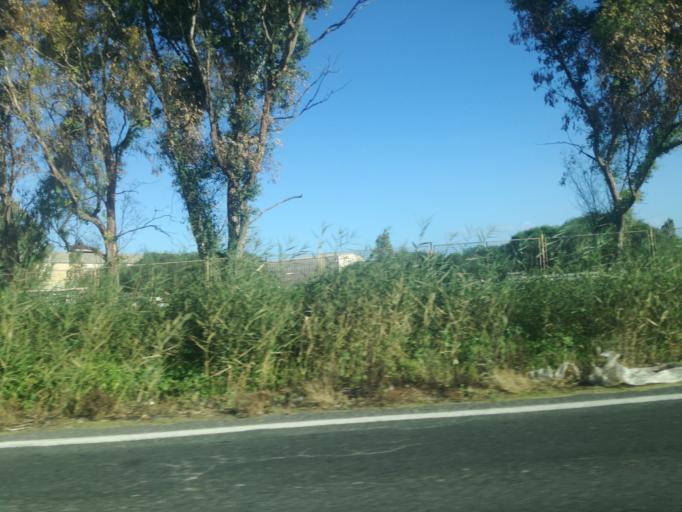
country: IT
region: Sicily
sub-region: Provincia di Caltanissetta
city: Gela
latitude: 37.0561
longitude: 14.2952
